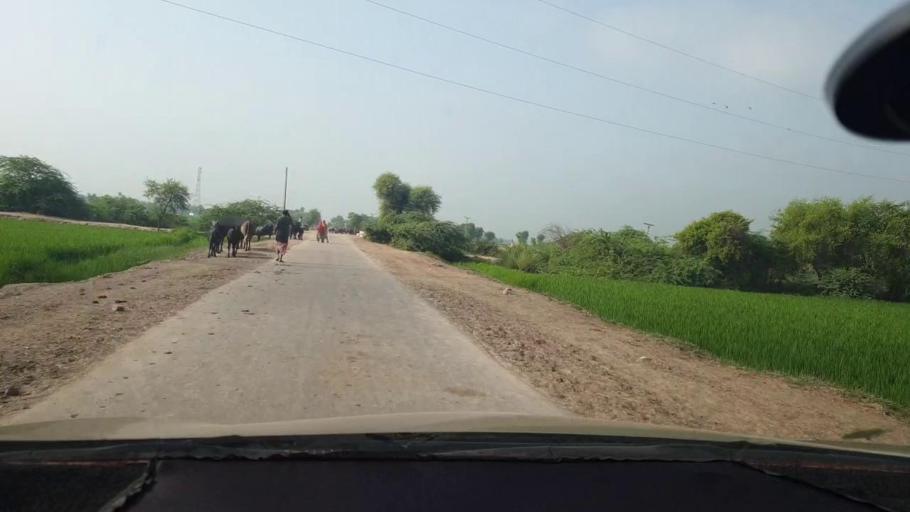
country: PK
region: Sindh
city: Goth Garelo
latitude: 27.4957
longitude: 68.0110
